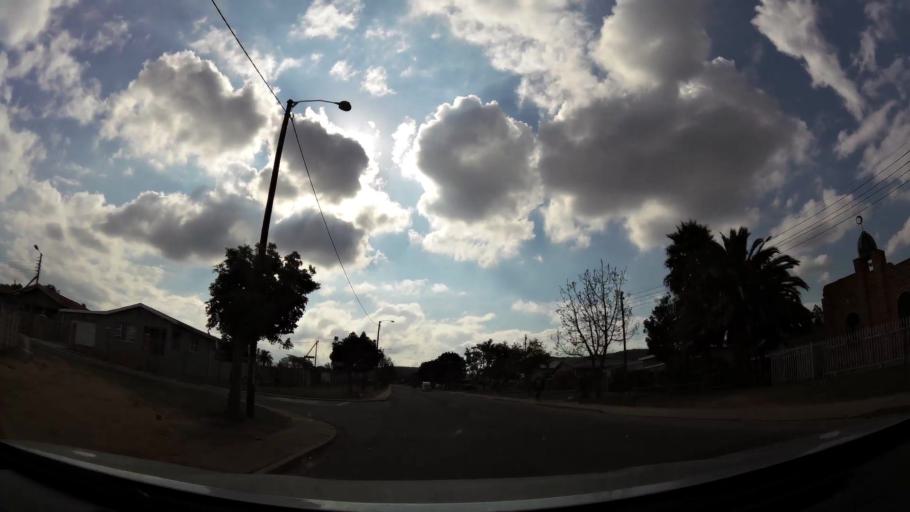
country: ZA
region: Eastern Cape
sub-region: Nelson Mandela Bay Metropolitan Municipality
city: Uitenhage
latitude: -33.7359
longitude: 25.3809
